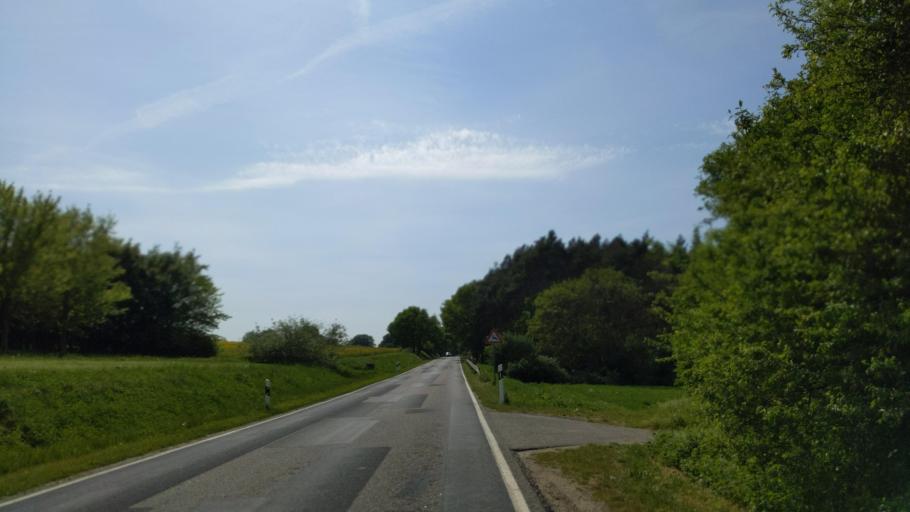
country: DE
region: Mecklenburg-Vorpommern
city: Selmsdorf
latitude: 53.8785
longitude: 10.8504
